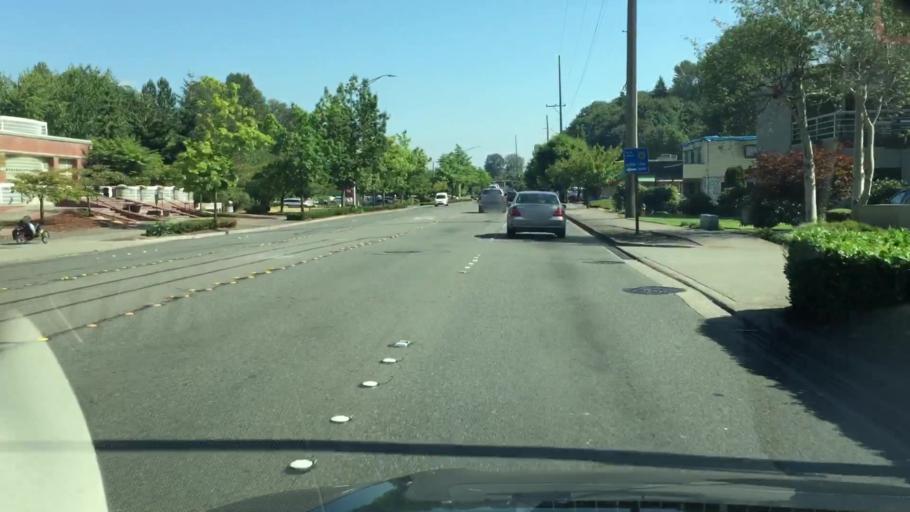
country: US
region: Washington
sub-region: King County
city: Tukwila
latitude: 47.4787
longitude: -122.2628
